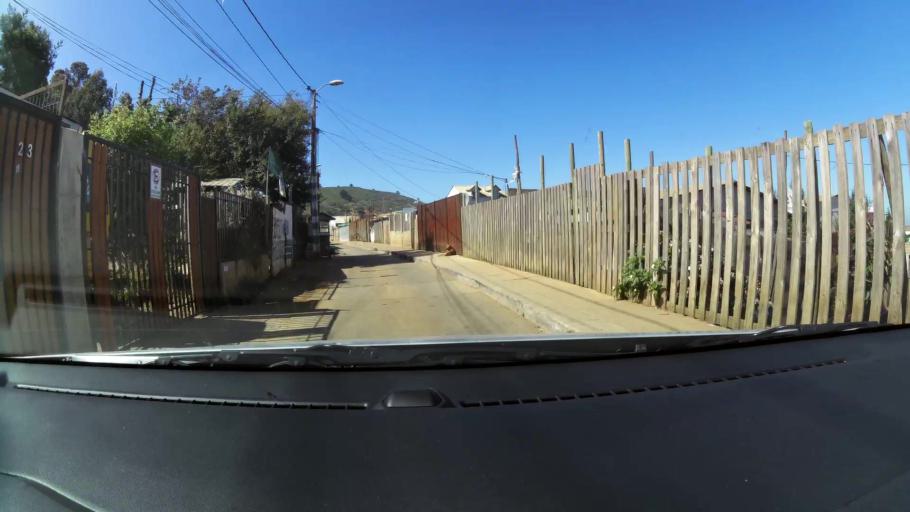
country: CL
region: Valparaiso
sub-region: Provincia de Valparaiso
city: Valparaiso
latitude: -33.0544
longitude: -71.6503
